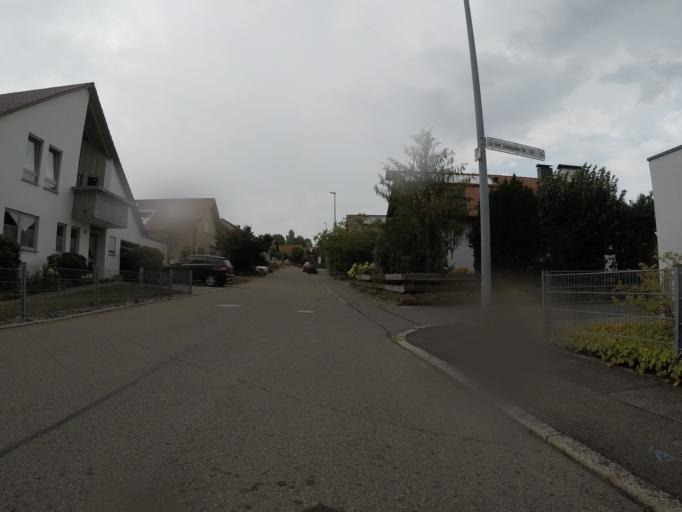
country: DE
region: Baden-Wuerttemberg
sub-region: Tuebingen Region
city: Eningen unter Achalm
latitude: 48.4871
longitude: 9.2465
